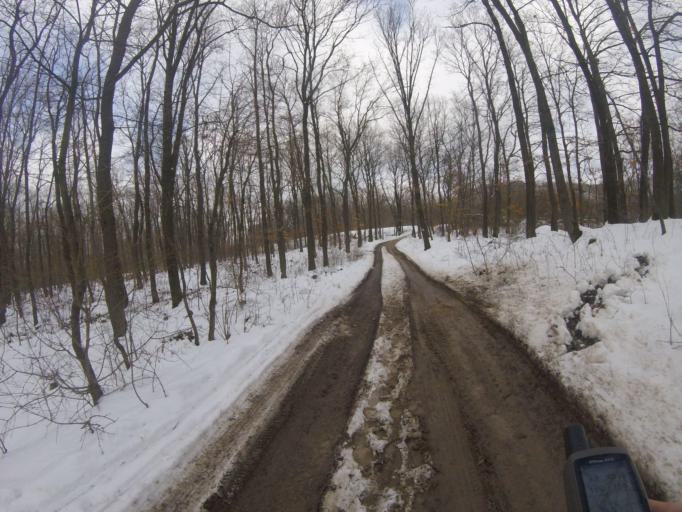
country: HU
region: Pest
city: Pilisszentkereszt
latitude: 47.6988
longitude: 18.8952
